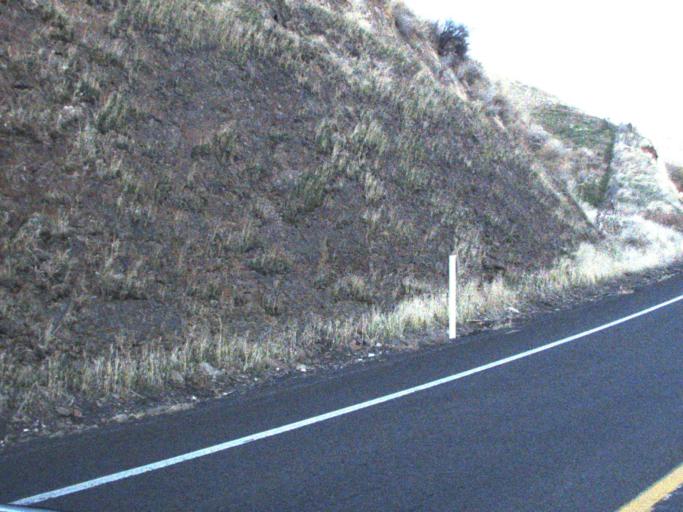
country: US
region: Washington
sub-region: Garfield County
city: Pomeroy
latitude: 46.6504
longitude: -117.8068
